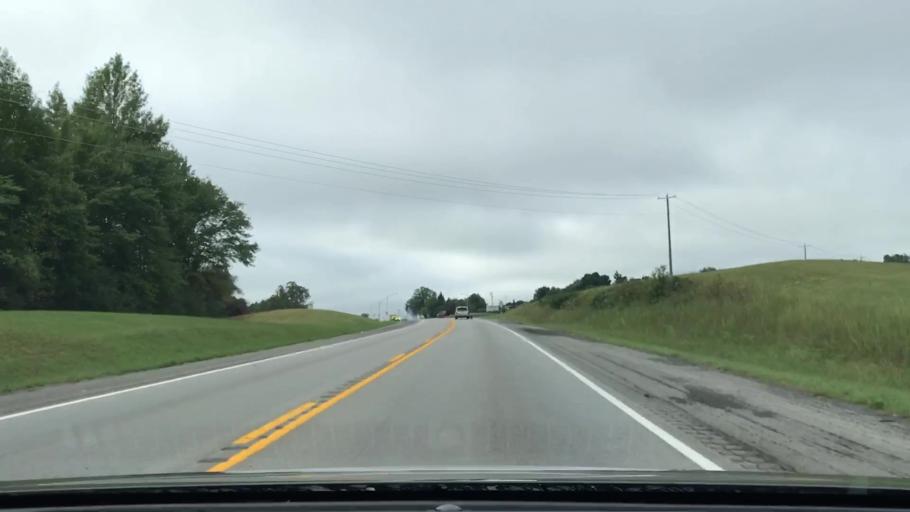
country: US
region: Kentucky
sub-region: Russell County
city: Russell Springs
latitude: 37.0413
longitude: -85.0731
